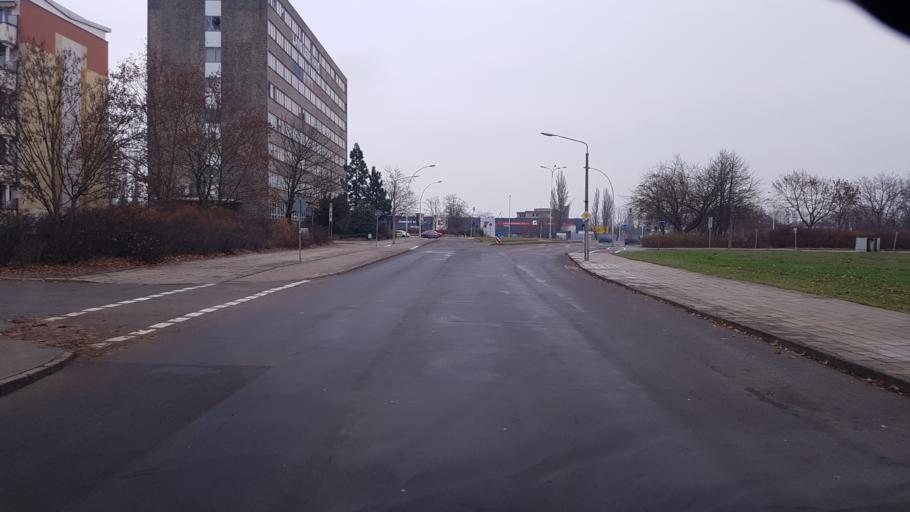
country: DE
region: Brandenburg
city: Eisenhuettenstadt
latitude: 52.1412
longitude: 14.6481
